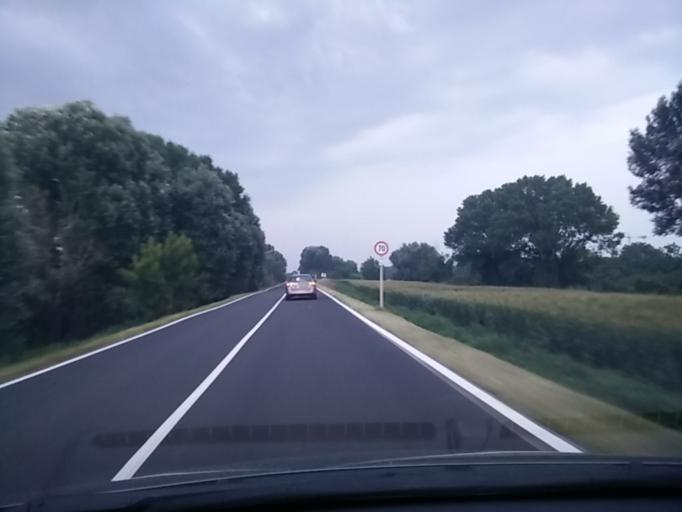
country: IT
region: Veneto
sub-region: Provincia di Venezia
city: Passarella
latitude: 45.5938
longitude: 12.6256
